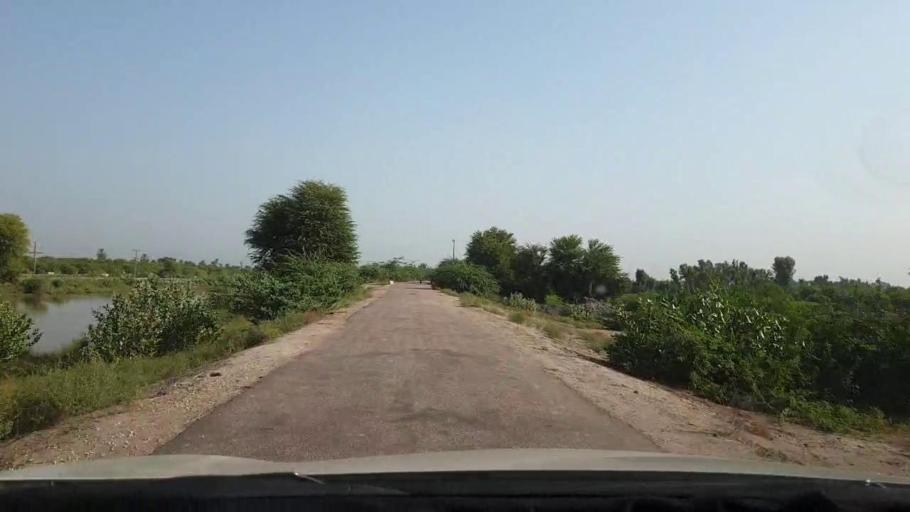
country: PK
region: Sindh
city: Larkana
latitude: 27.5526
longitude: 68.2563
